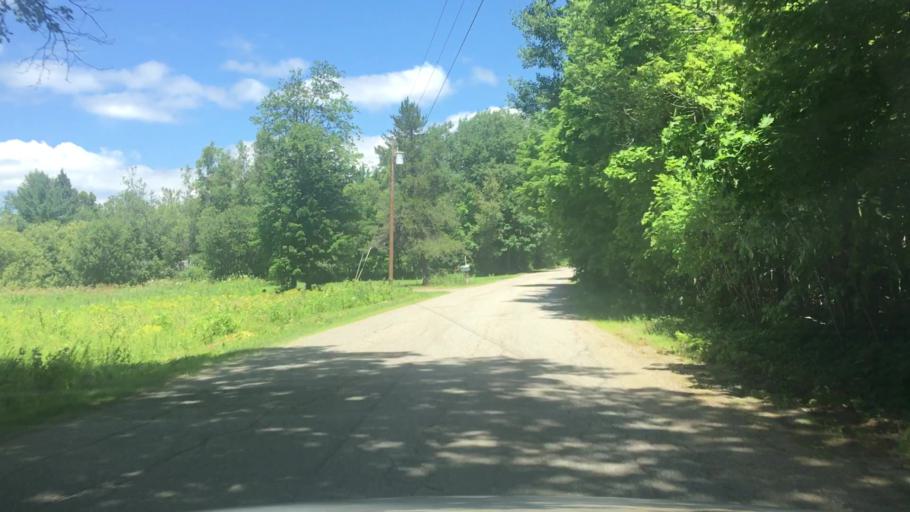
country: US
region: Maine
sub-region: Kennebec County
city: Albion
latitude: 44.4572
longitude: -69.3139
